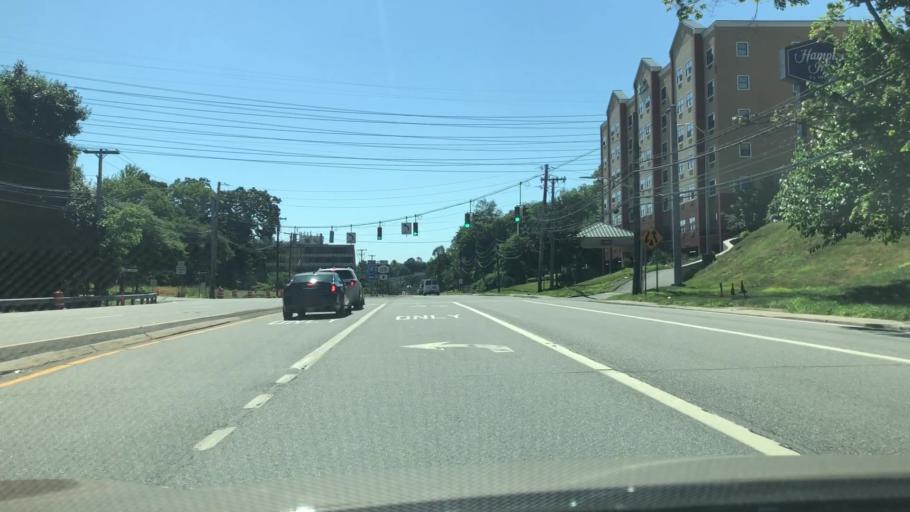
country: US
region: New York
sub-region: Westchester County
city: Elmsford
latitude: 41.0585
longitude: -73.8272
